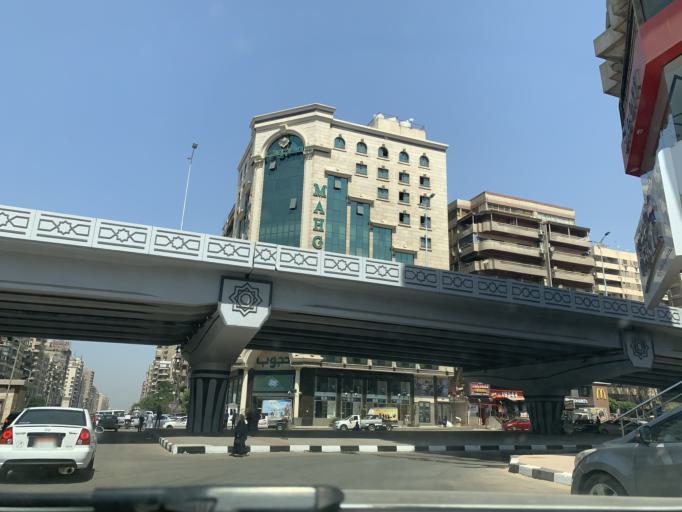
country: EG
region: Muhafazat al Qahirah
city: Cairo
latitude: 30.0543
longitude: 31.3463
